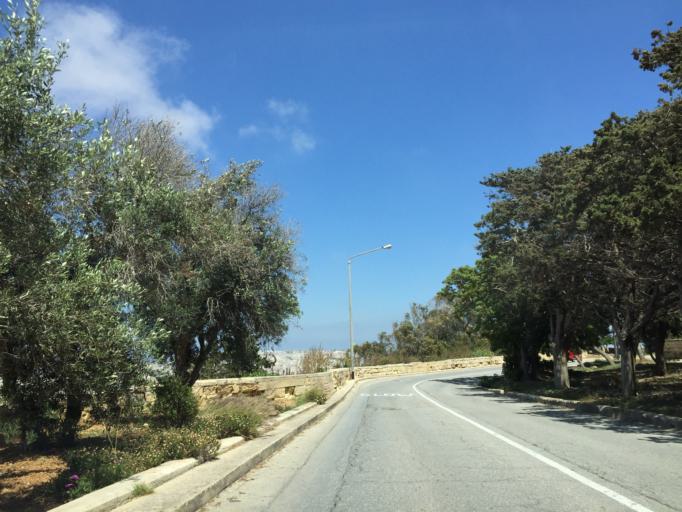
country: MT
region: L-Imtarfa
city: Imtarfa
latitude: 35.8957
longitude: 14.4021
